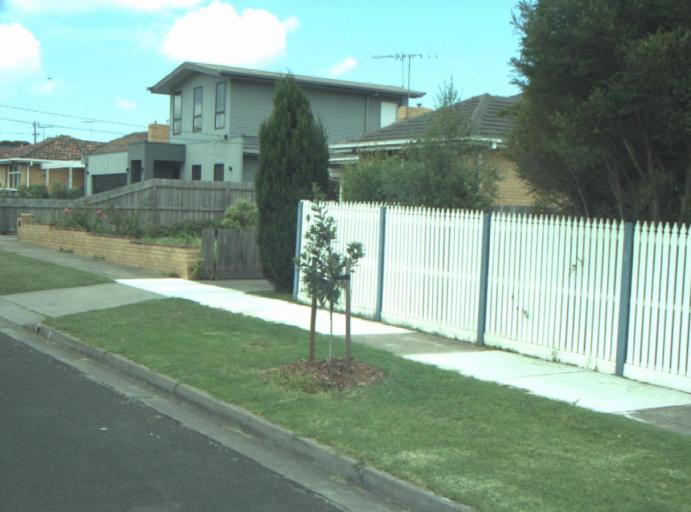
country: AU
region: Victoria
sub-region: Greater Geelong
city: Wandana Heights
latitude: -38.1816
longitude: 144.3265
